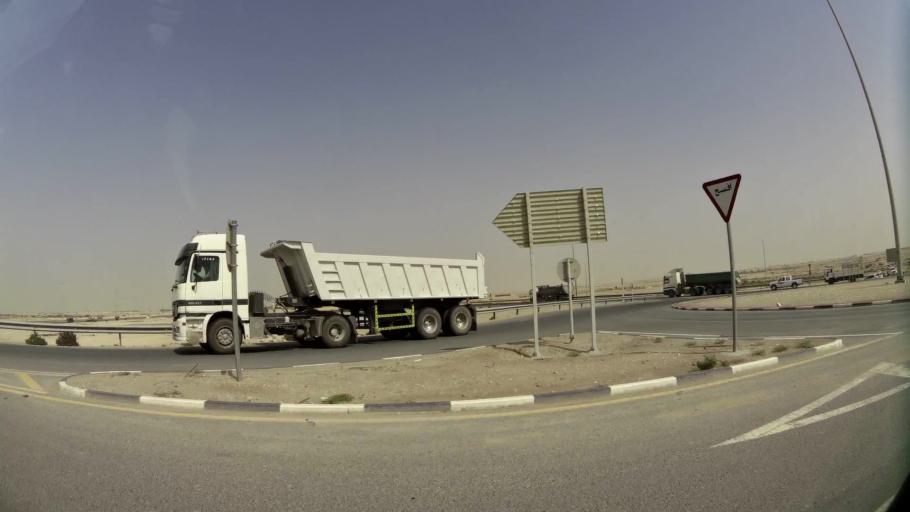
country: QA
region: Baladiyat ar Rayyan
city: Ar Rayyan
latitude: 25.1528
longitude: 51.2781
